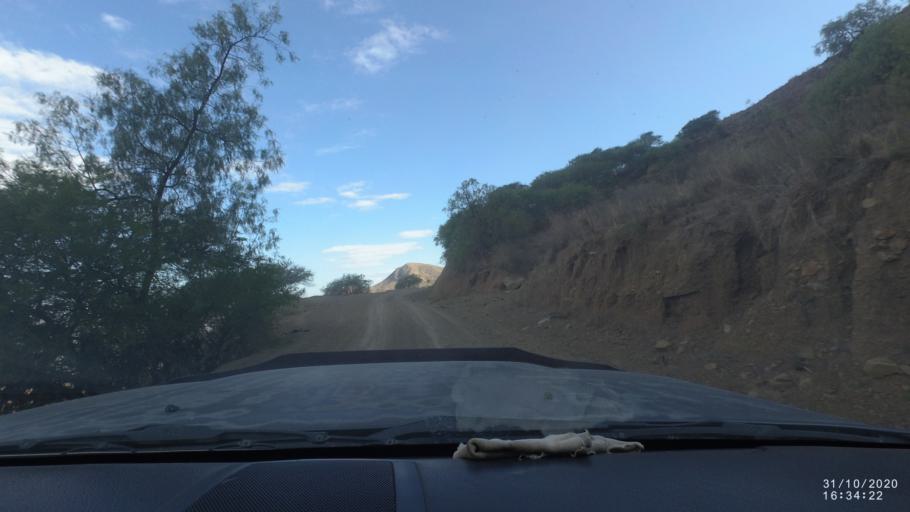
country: BO
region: Chuquisaca
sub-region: Provincia Zudanez
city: Mojocoya
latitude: -18.4480
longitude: -64.5847
